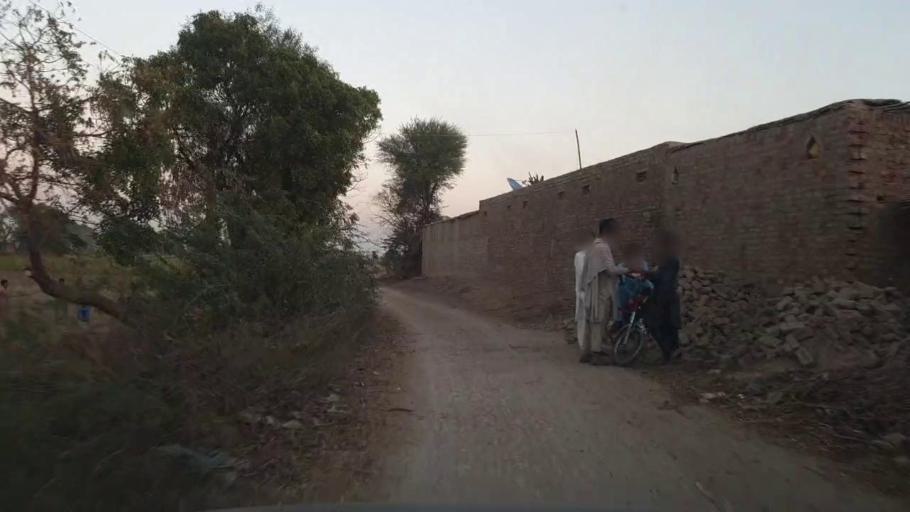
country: PK
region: Sindh
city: Chambar
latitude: 25.3381
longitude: 68.7621
